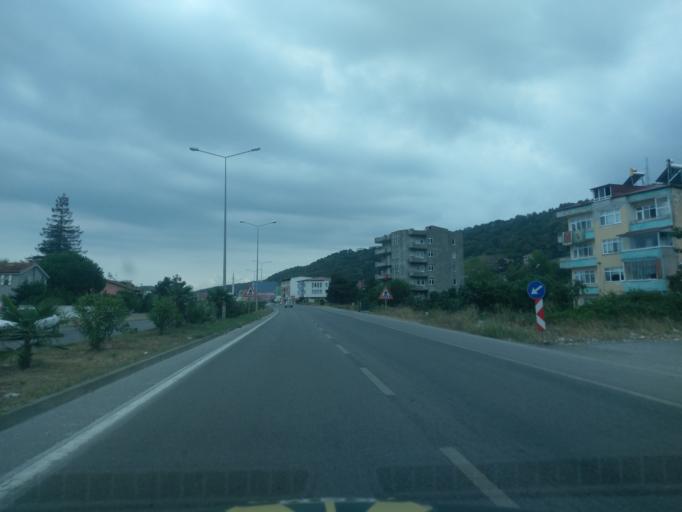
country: TR
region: Samsun
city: Taflan
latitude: 41.3896
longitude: 36.2034
